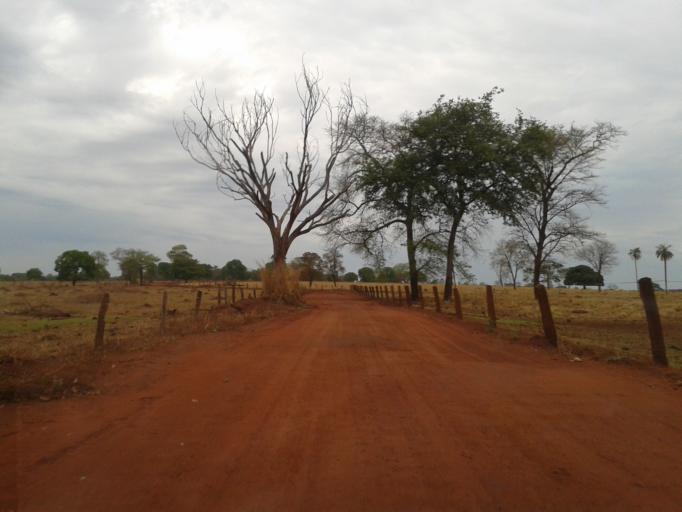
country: BR
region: Minas Gerais
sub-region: Capinopolis
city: Capinopolis
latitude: -18.9138
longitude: -49.7530
